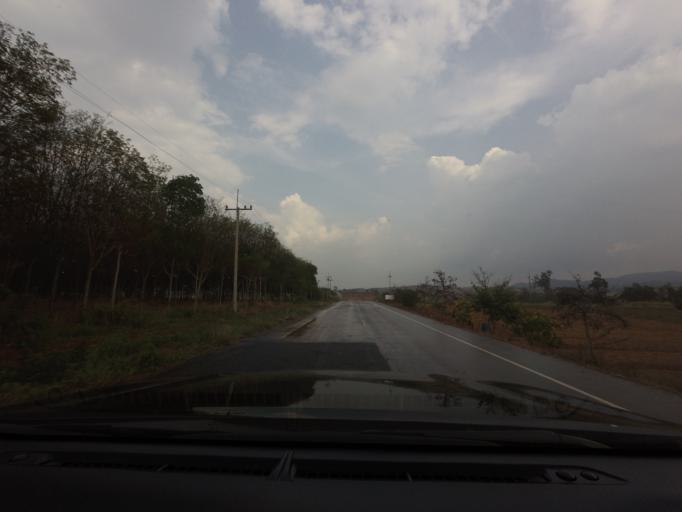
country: TH
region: Nakhon Ratchasima
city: Wang Nam Khiao
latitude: 14.4098
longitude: 101.7424
